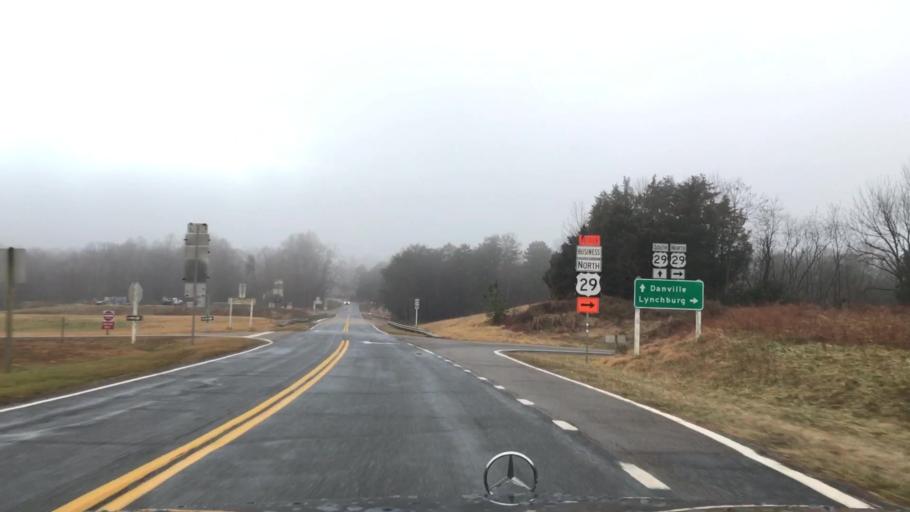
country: US
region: Virginia
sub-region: Pittsylvania County
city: Hurt
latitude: 37.1145
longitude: -79.3249
